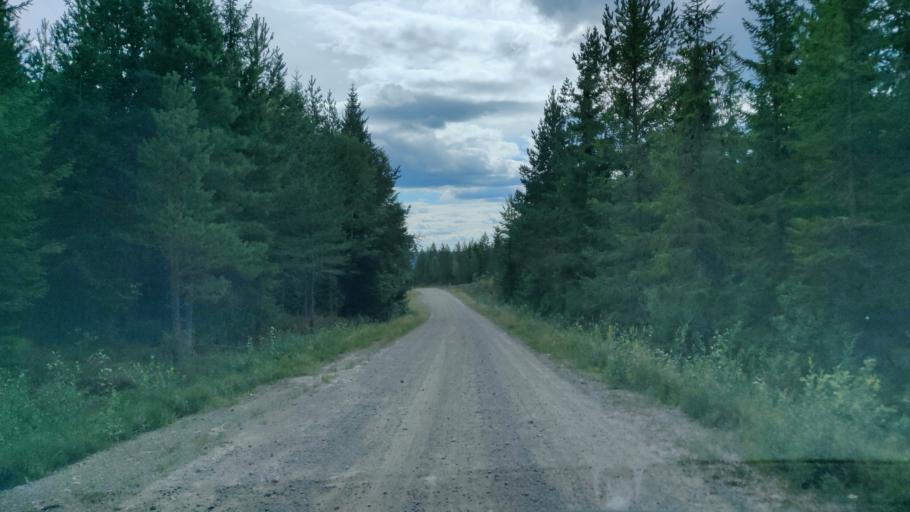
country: SE
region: Vaermland
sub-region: Hagfors Kommun
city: Hagfors
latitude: 60.0163
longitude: 13.7298
